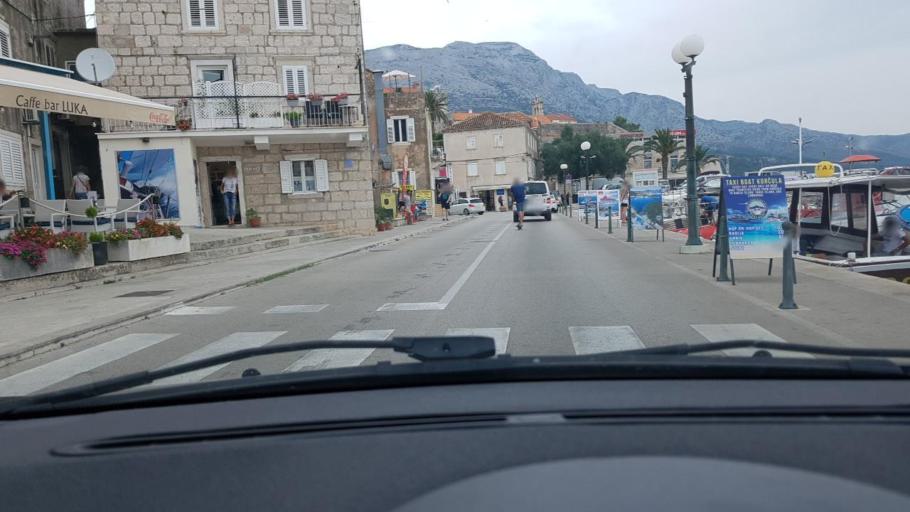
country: HR
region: Dubrovacko-Neretvanska
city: Korcula
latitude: 42.9597
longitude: 17.1356
